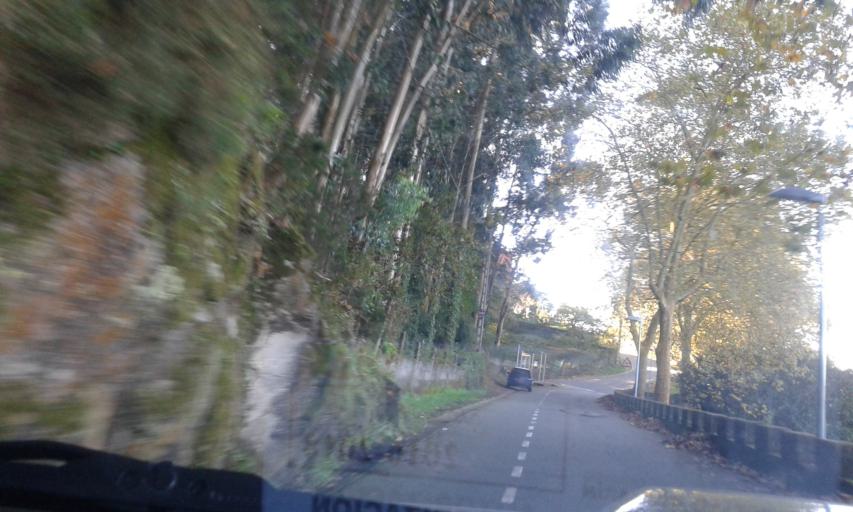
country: ES
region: Galicia
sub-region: Provincia de Pontevedra
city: Marin
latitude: 42.3890
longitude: -8.7167
